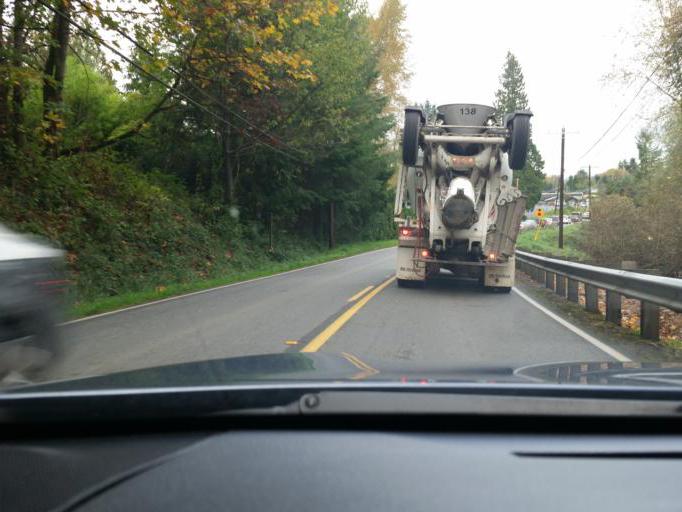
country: US
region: Washington
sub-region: Snohomish County
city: Cathcart
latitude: 47.8458
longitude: -122.1014
